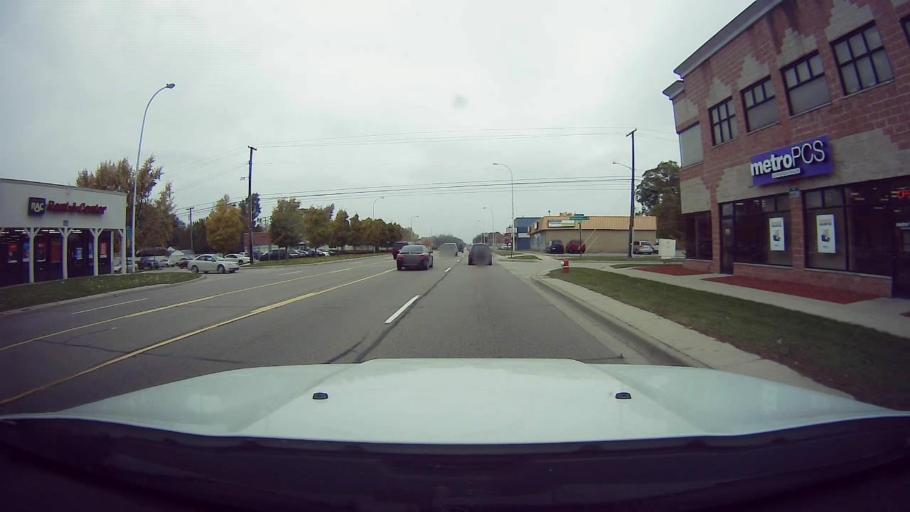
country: US
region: Michigan
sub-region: Oakland County
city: Madison Heights
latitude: 42.4927
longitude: -83.1053
